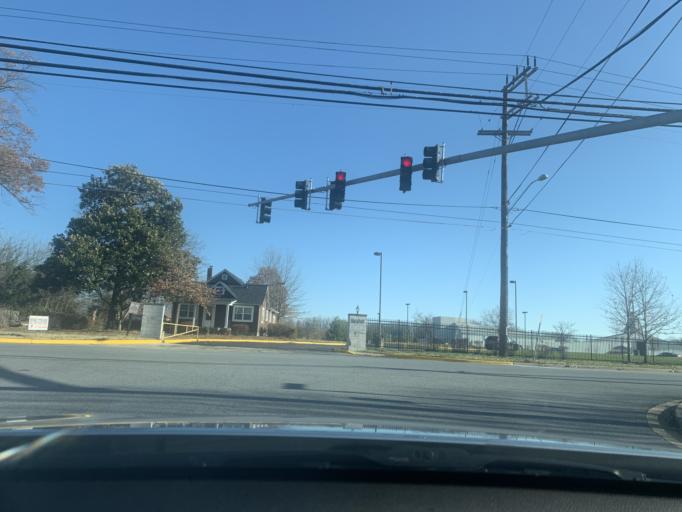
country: US
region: Maryland
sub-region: Prince George's County
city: Camp Springs
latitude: 38.8129
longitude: -76.9154
